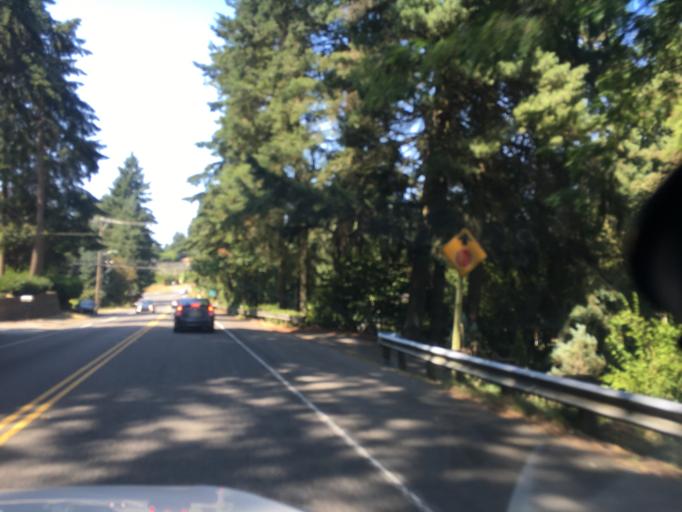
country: US
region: Washington
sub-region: King County
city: Shoreline
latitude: 47.7480
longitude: -122.3535
